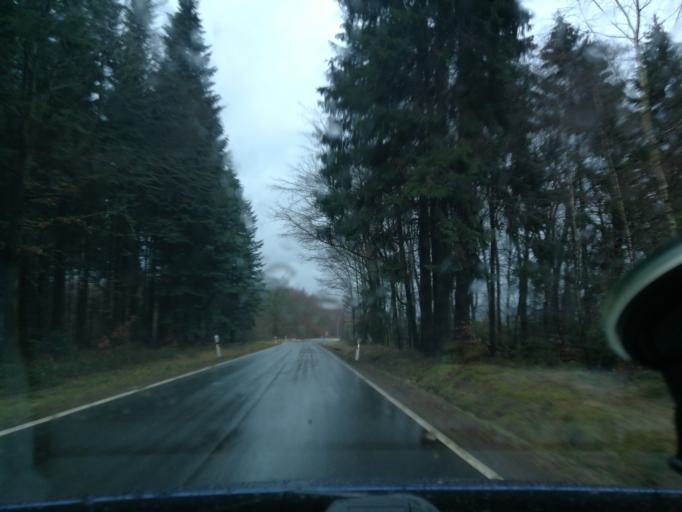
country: DE
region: Rheinland-Pfalz
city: Deuselbach
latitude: 49.7478
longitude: 7.0420
